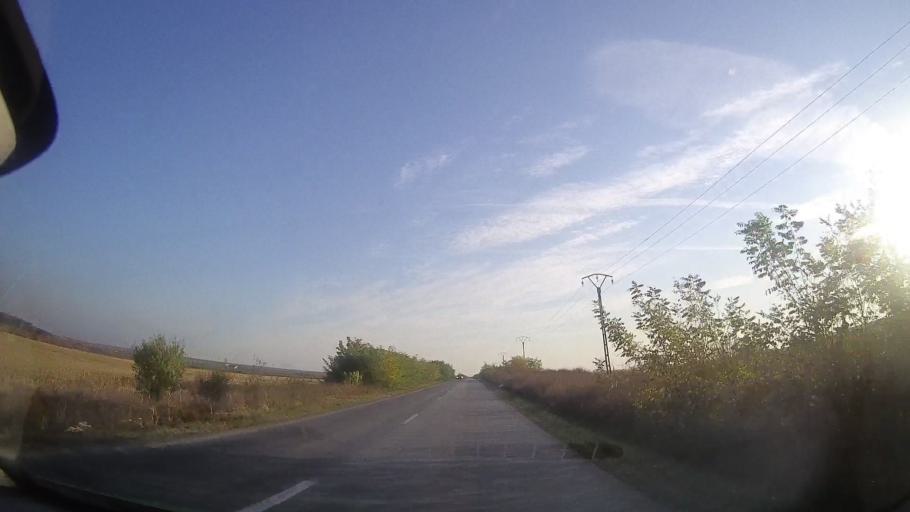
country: RO
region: Timis
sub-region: Comuna Pischia
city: Pischia
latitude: 45.8803
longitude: 21.3368
